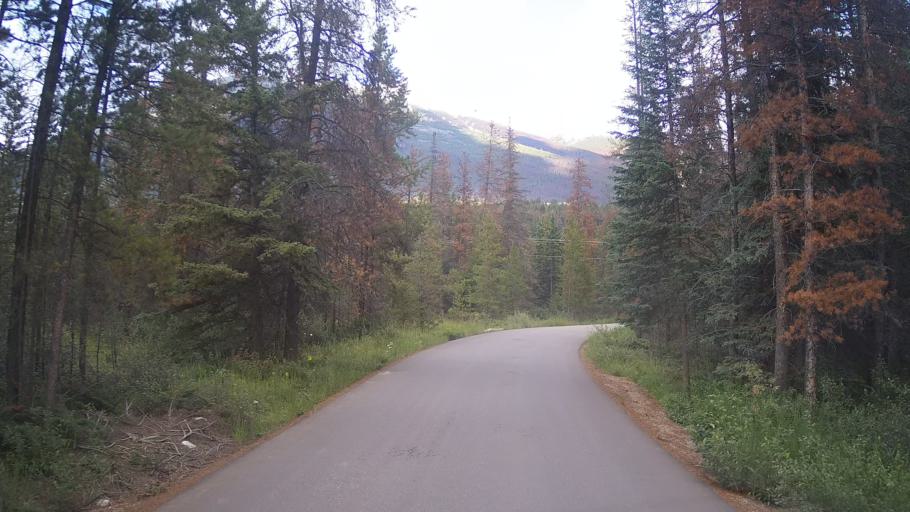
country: CA
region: Alberta
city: Jasper Park Lodge
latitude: 52.9202
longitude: -118.0210
